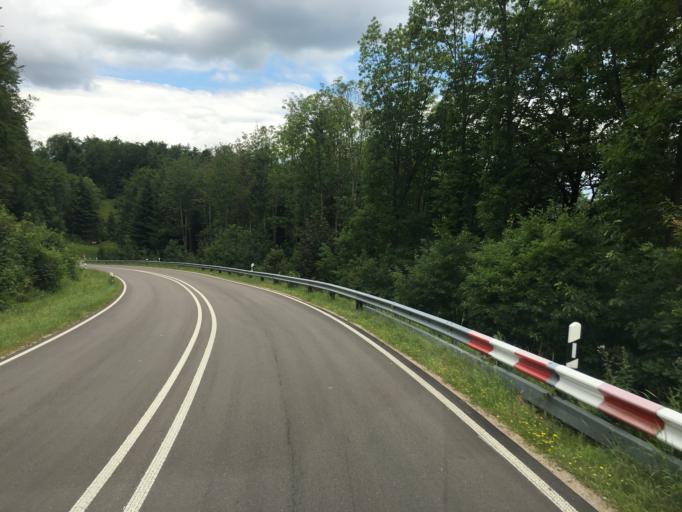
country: DE
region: Baden-Wuerttemberg
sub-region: Karlsruhe Region
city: Baden-Baden
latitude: 48.7122
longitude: 8.2386
